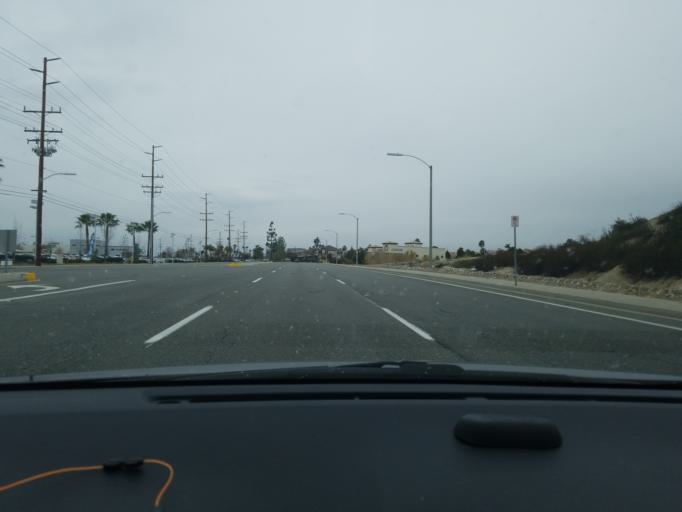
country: US
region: California
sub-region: Riverside County
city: Temecula
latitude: 33.5080
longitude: -117.1504
